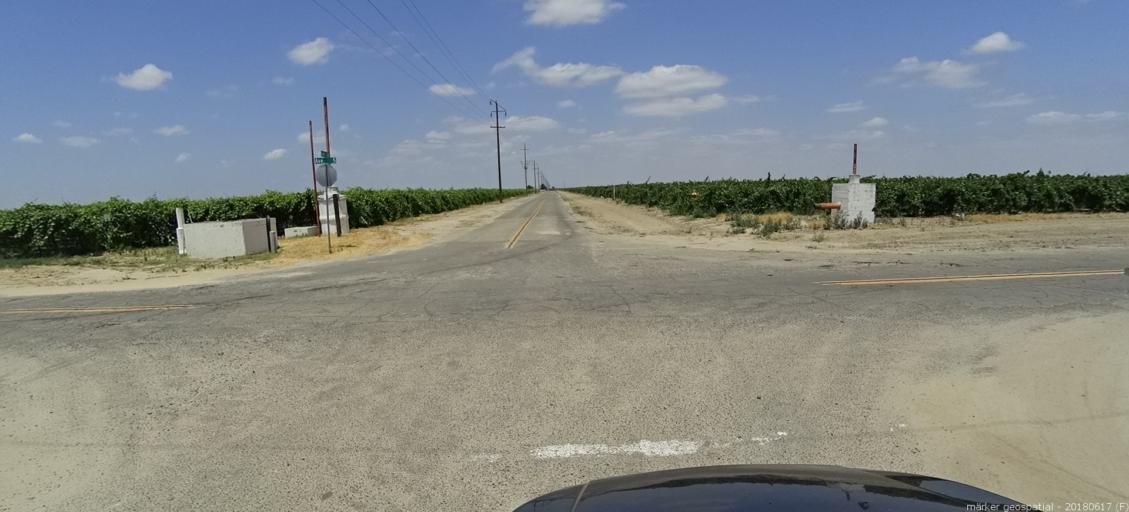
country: US
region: California
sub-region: Fresno County
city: Biola
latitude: 36.8221
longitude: -120.1149
